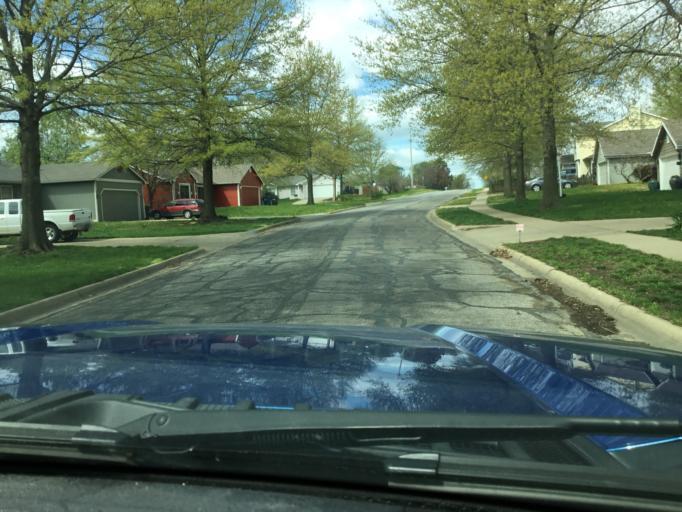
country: US
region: Kansas
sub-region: Douglas County
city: Lawrence
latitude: 38.9387
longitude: -95.2128
